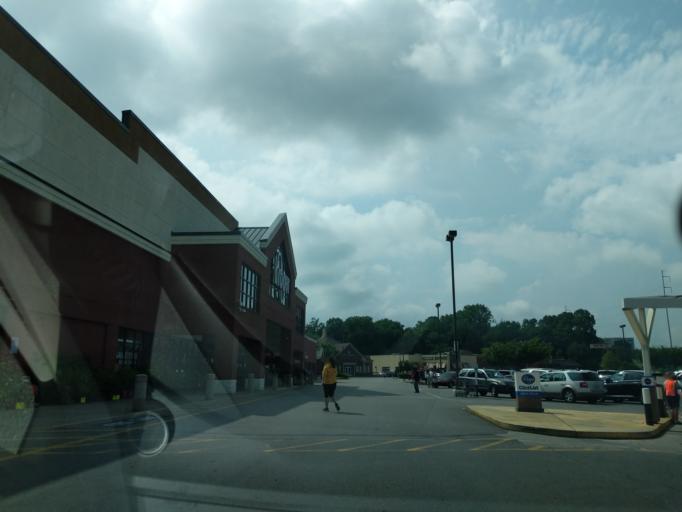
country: US
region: Tennessee
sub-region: Davidson County
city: Lakewood
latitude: 36.1822
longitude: -86.6058
